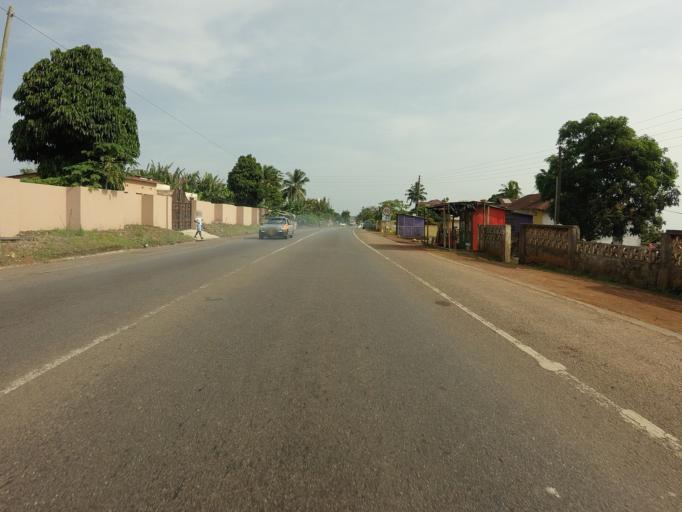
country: GH
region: Eastern
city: Aburi
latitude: 5.8706
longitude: -0.1589
